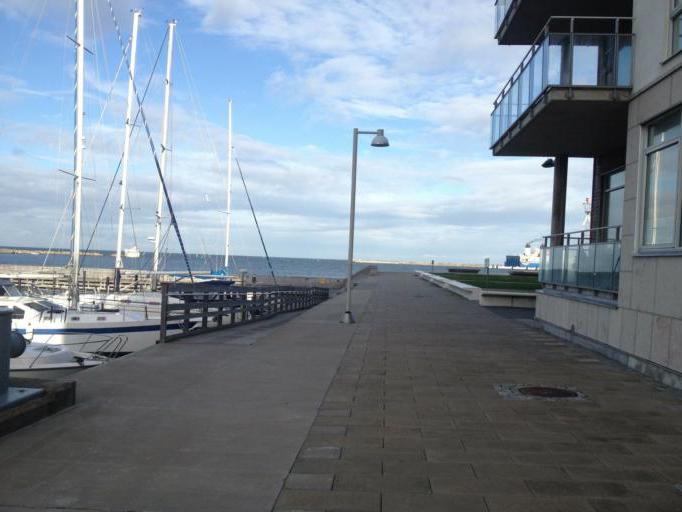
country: SE
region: Skane
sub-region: Malmo
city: Malmoe
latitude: 55.6182
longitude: 12.9889
